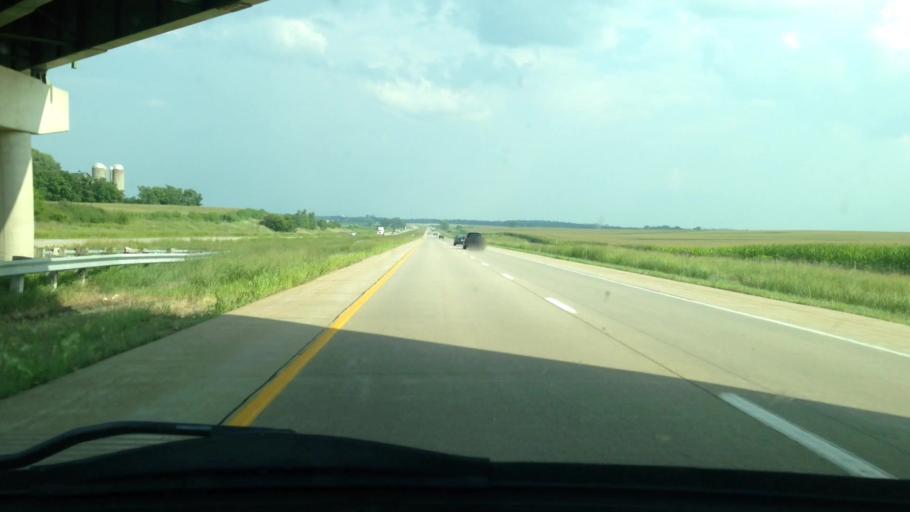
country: US
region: Iowa
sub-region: Black Hawk County
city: La Porte City
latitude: 42.3846
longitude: -92.1248
